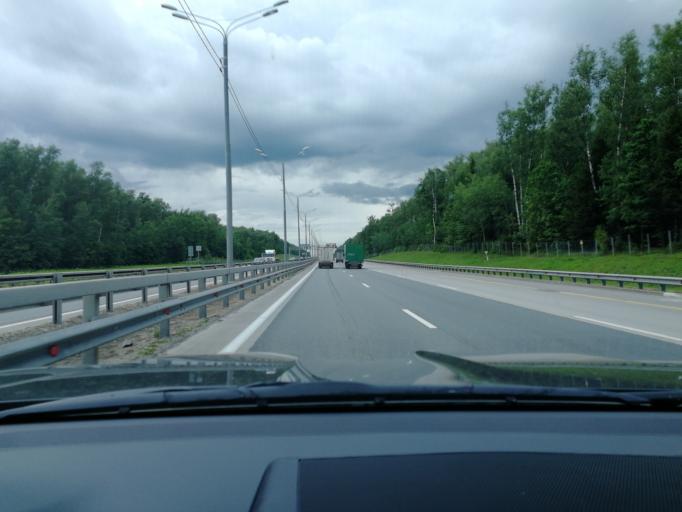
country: RU
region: Moskovskaya
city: Belyye Stolby
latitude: 55.2918
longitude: 37.8486
